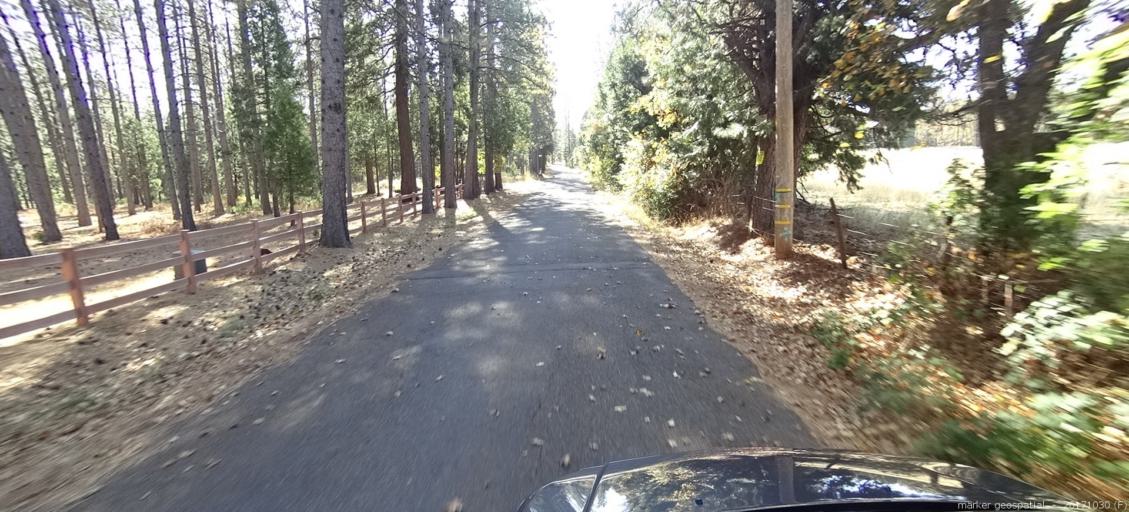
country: US
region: California
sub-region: Shasta County
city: Shingletown
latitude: 40.6305
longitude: -121.8950
